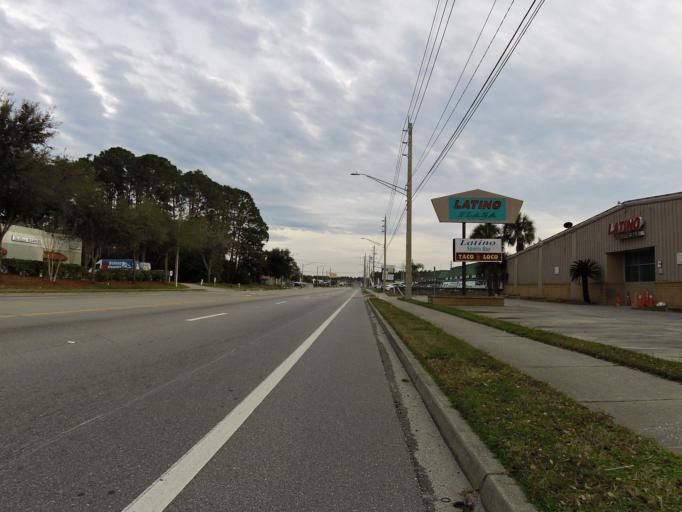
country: US
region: Florida
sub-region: Duval County
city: Jacksonville
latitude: 30.2622
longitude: -81.6212
